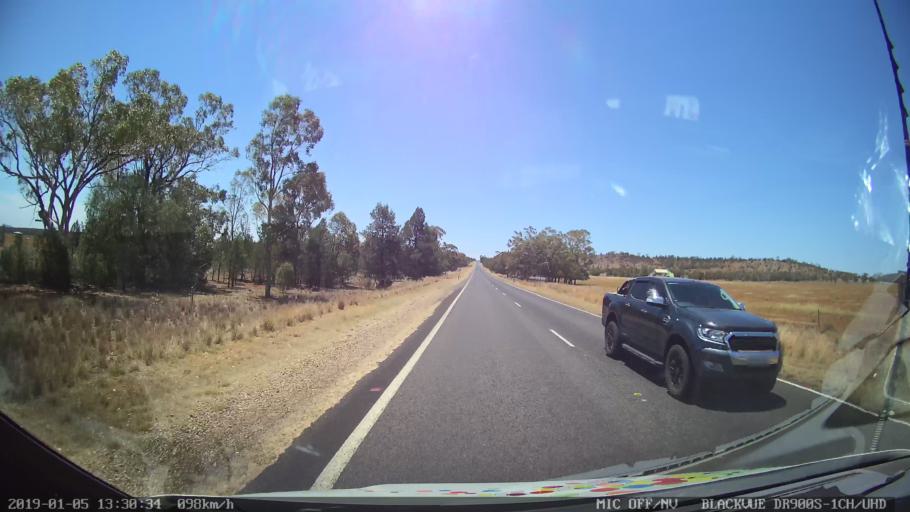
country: AU
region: New South Wales
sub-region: Gunnedah
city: Gunnedah
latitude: -31.0178
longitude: 150.0724
